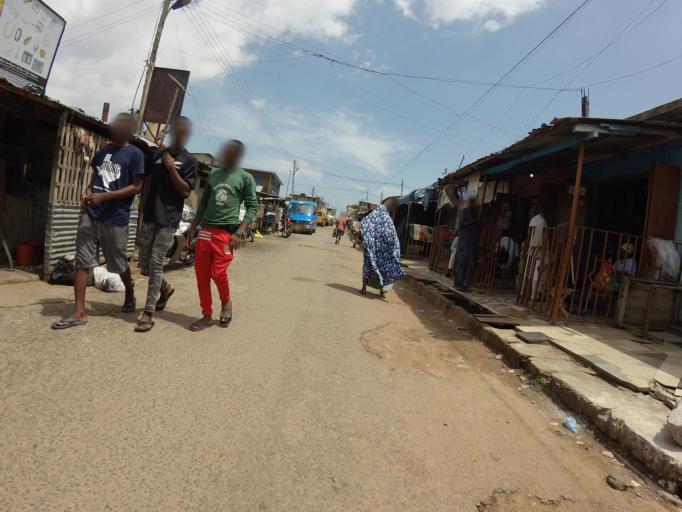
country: GH
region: Greater Accra
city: Accra
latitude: 5.5824
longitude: -0.1999
